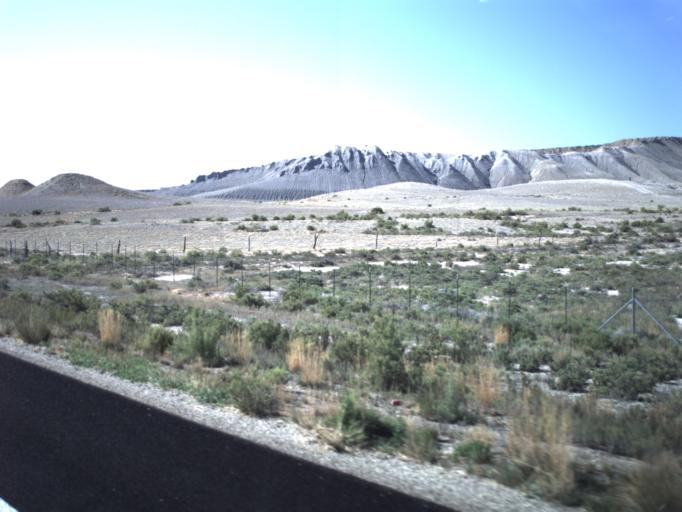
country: US
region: Utah
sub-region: Emery County
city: Ferron
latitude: 39.0596
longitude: -111.1288
